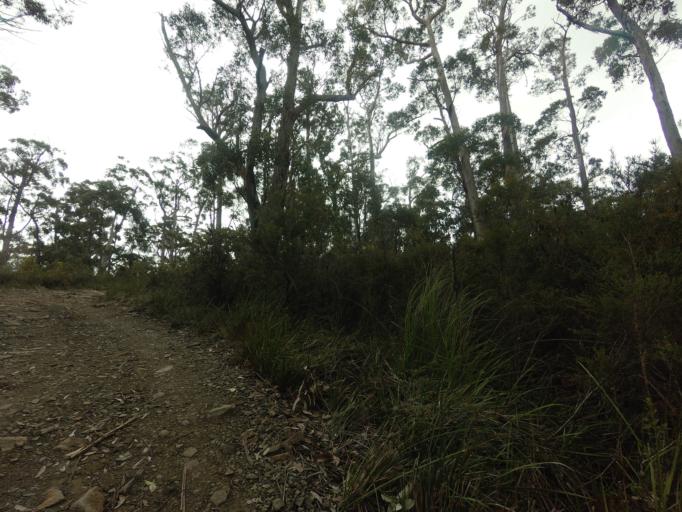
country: AU
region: Tasmania
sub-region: Huon Valley
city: Geeveston
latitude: -43.4719
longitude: 146.9318
